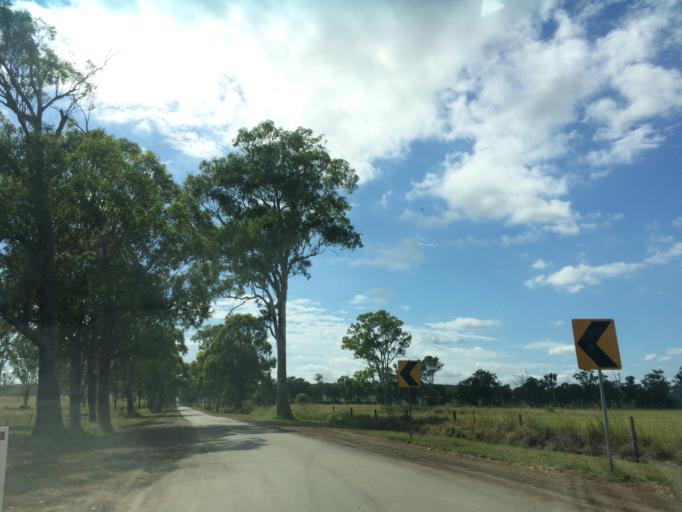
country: AU
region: Queensland
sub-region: Logan
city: Cedar Vale
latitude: -27.8799
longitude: 152.9554
